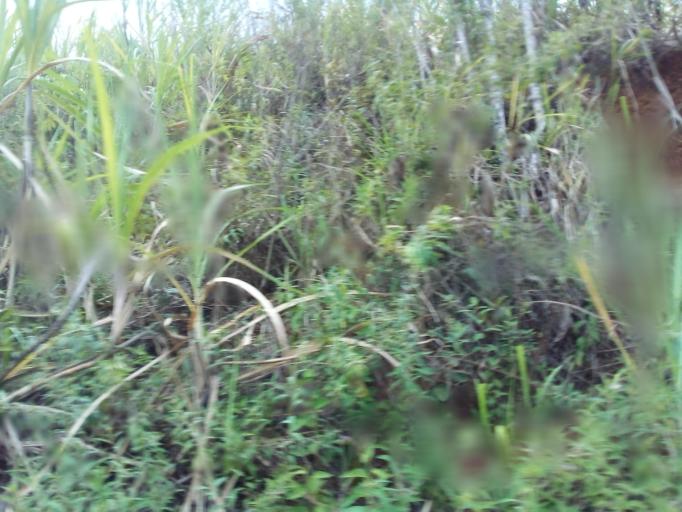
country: BR
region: Espirito Santo
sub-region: Ibiracu
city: Ibiracu
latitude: -19.7967
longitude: -40.3691
